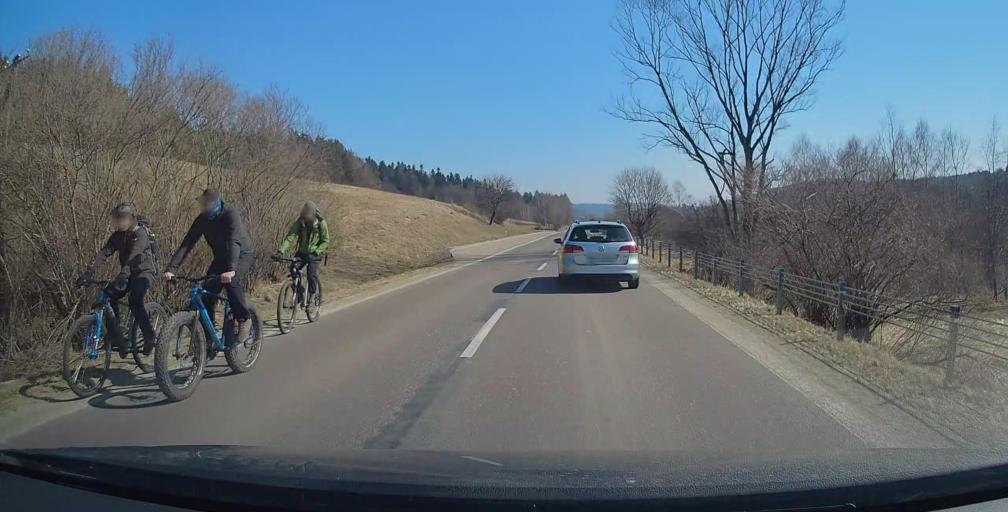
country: PL
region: Subcarpathian Voivodeship
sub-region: Powiat przemyski
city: Bircza
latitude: 49.5951
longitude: 22.5158
